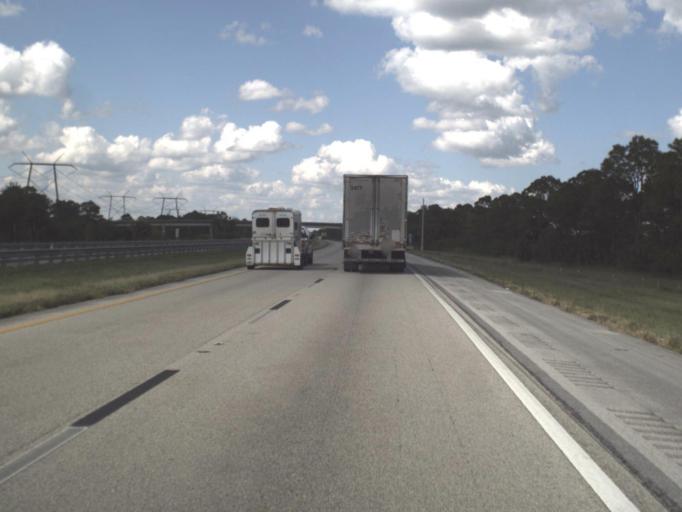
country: US
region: Florida
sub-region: Indian River County
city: West Vero Corridor
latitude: 27.5315
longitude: -80.6068
